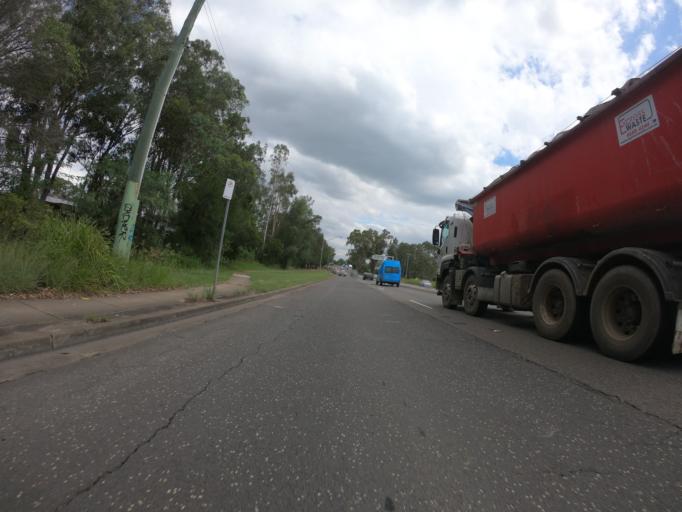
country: AU
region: New South Wales
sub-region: Blacktown
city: Mount Druitt
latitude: -33.7864
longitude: 150.7707
